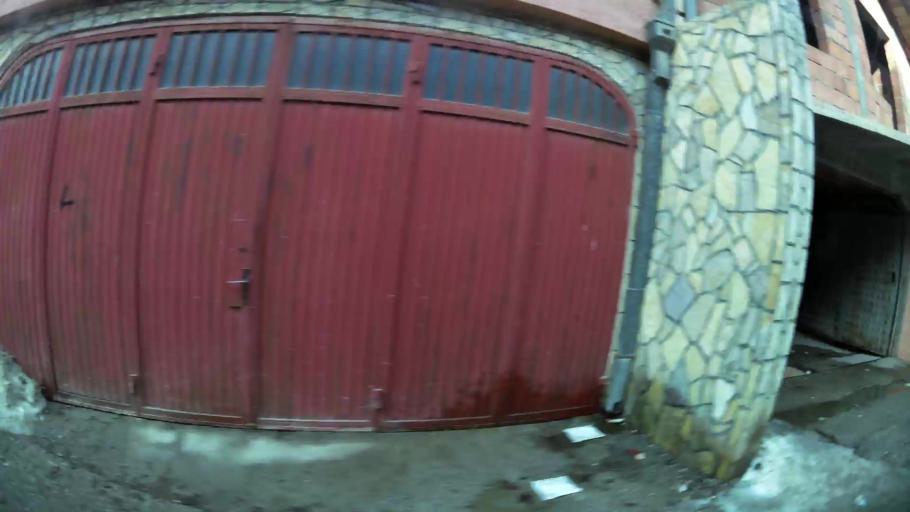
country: XK
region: Pristina
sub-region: Komuna e Prishtines
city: Pristina
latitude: 42.6727
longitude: 21.1753
